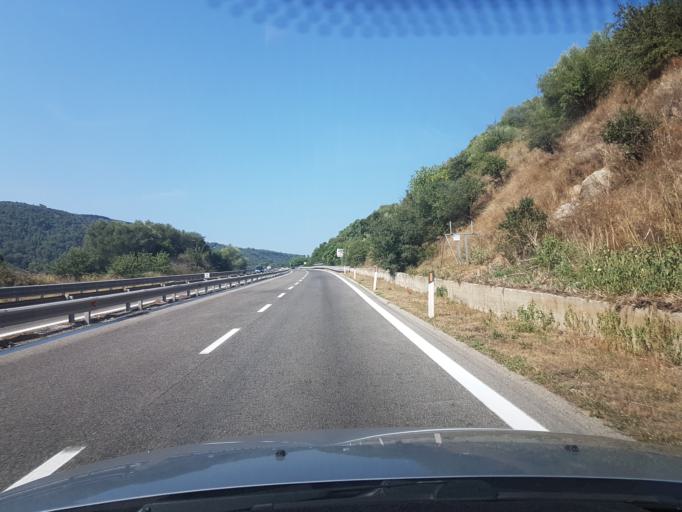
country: IT
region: Sardinia
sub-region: Provincia di Nuoro
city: Nuoro
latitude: 40.3423
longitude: 9.3129
